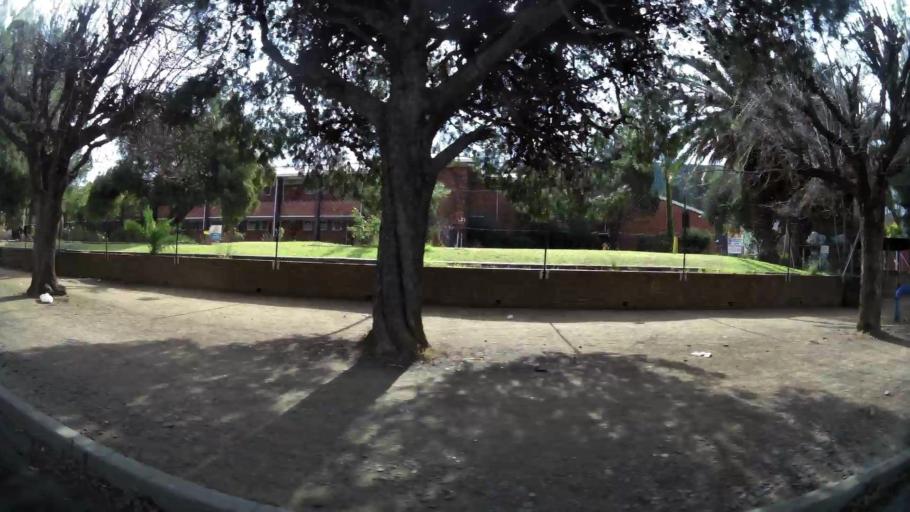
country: ZA
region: Orange Free State
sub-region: Mangaung Metropolitan Municipality
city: Bloemfontein
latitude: -29.1080
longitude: 26.2333
